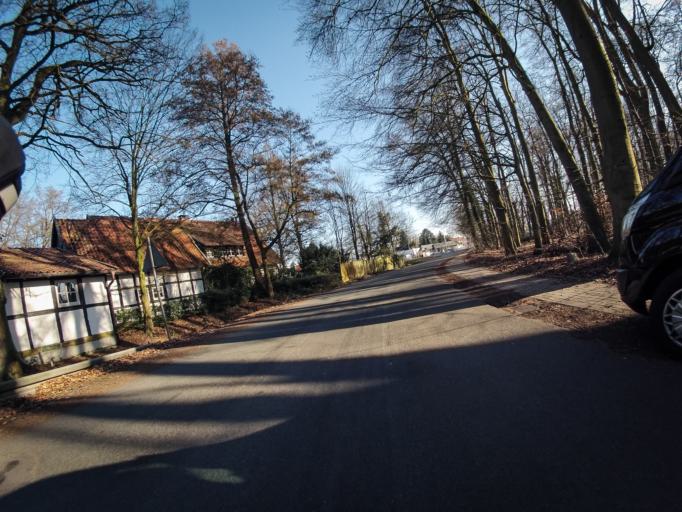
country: DE
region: Lower Saxony
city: Hasbergen
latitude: 52.2649
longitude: 7.9572
